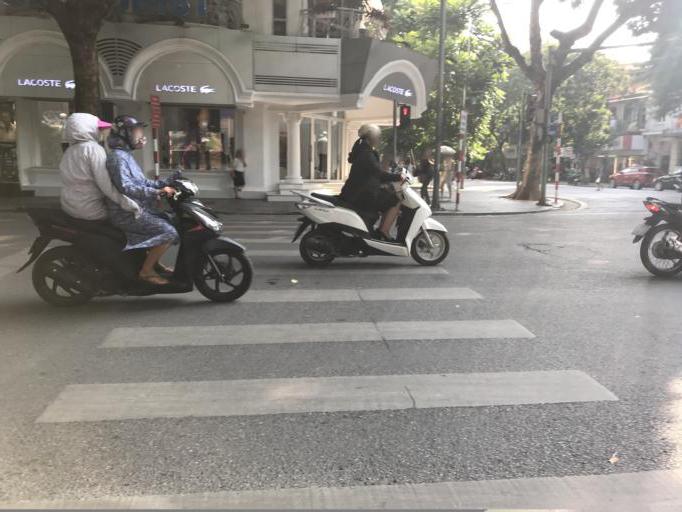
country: VN
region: Ha Noi
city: Hoan Kiem
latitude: 21.0260
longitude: 105.8519
